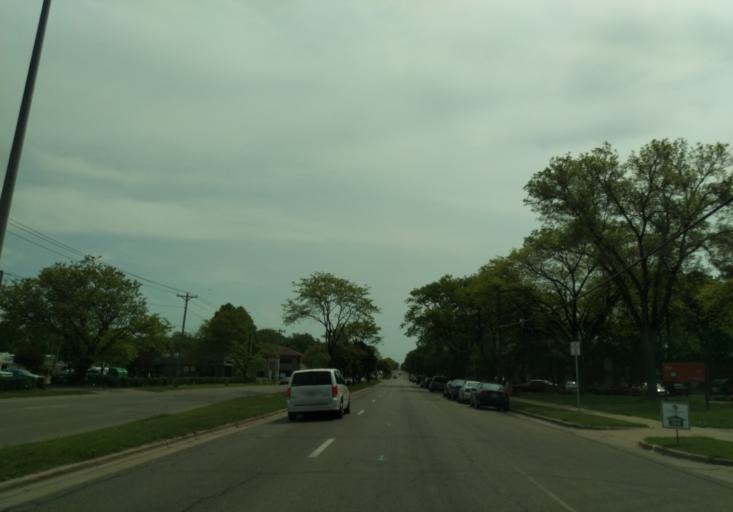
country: US
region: Wisconsin
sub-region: Dane County
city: Monona
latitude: 43.0842
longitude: -89.3023
